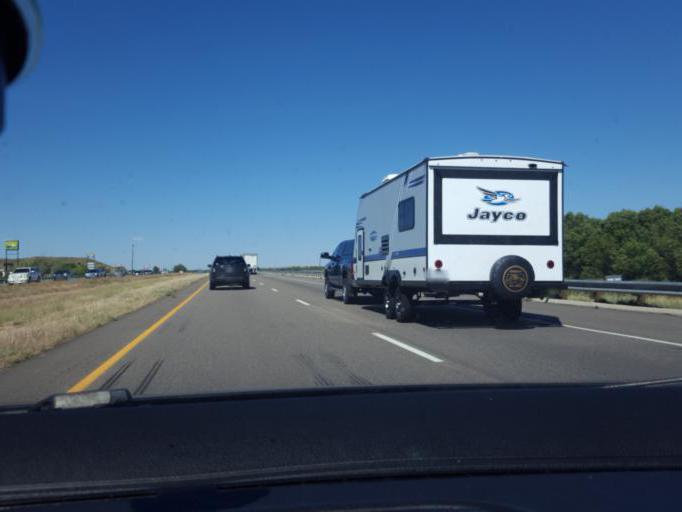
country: US
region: Colorado
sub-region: Pueblo County
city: Pueblo West
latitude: 38.4292
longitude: -104.6073
